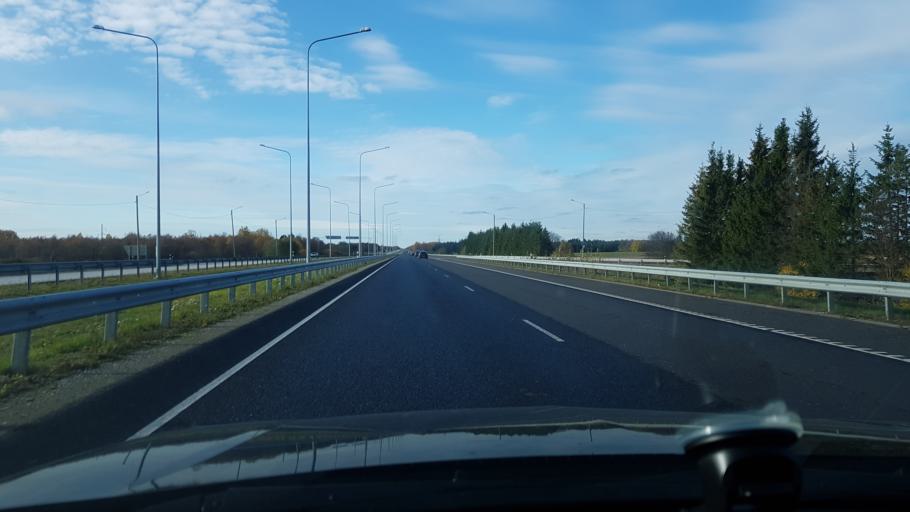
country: EE
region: Harju
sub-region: Kuusalu vald
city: Kuusalu
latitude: 59.4454
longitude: 25.3734
